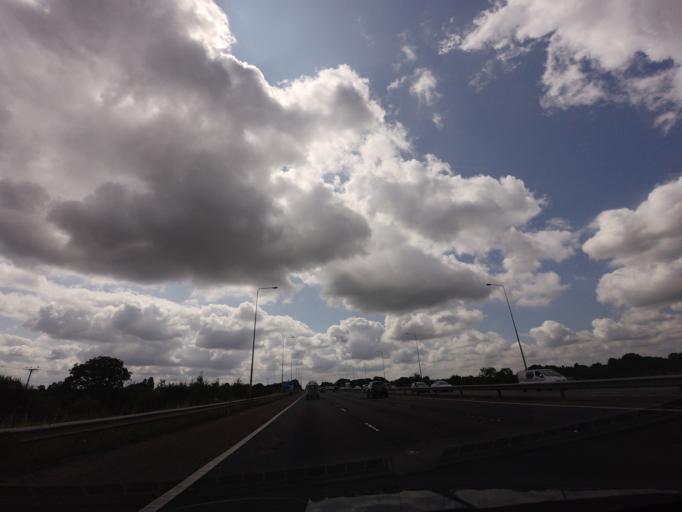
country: GB
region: England
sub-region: Borough of Wigan
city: Shevington
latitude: 53.6020
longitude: -2.6909
